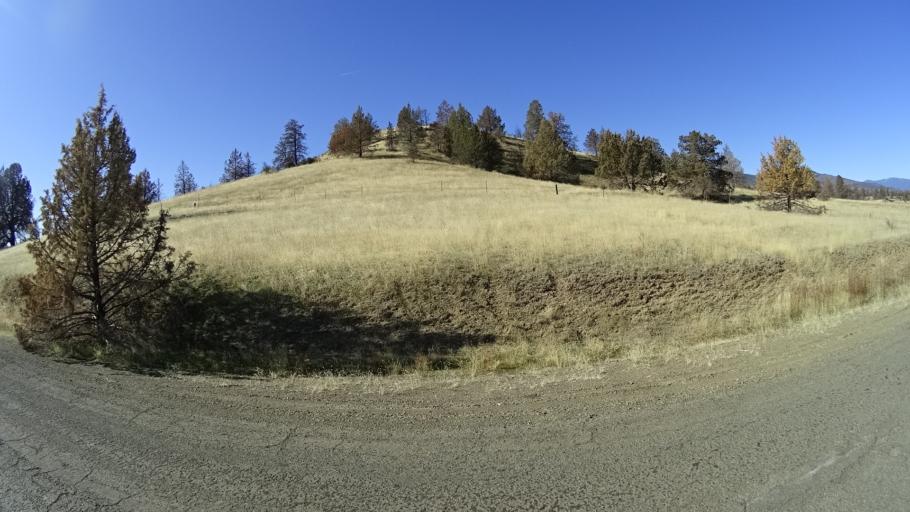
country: US
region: California
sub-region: Siskiyou County
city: Montague
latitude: 41.8918
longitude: -122.5499
